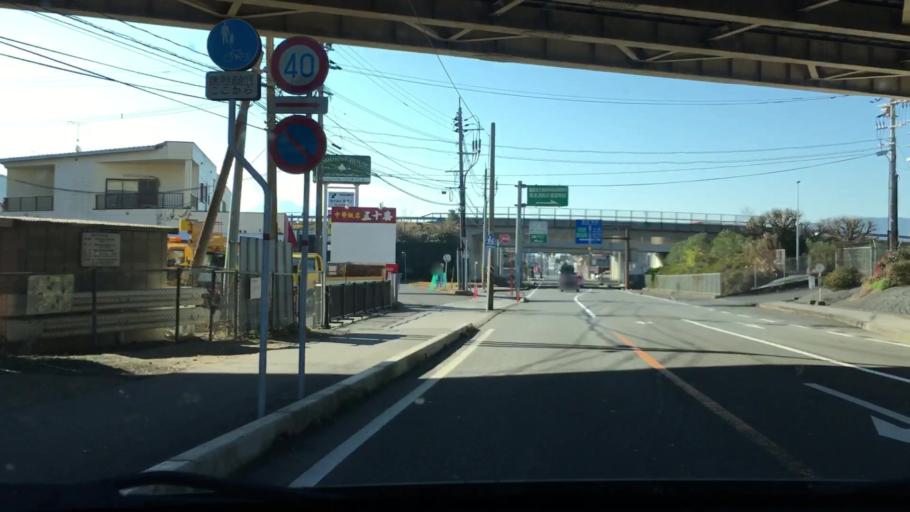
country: JP
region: Kagoshima
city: Kajiki
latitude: 31.7472
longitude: 130.6707
